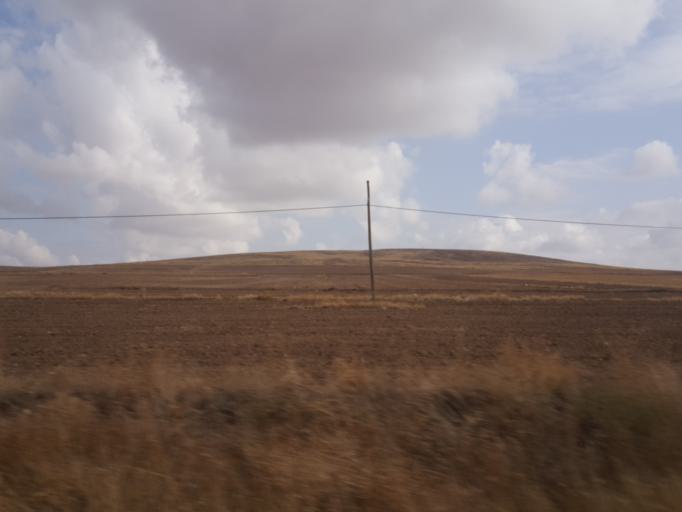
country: TR
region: Kirikkale
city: Keskin
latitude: 39.6288
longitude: 33.6102
